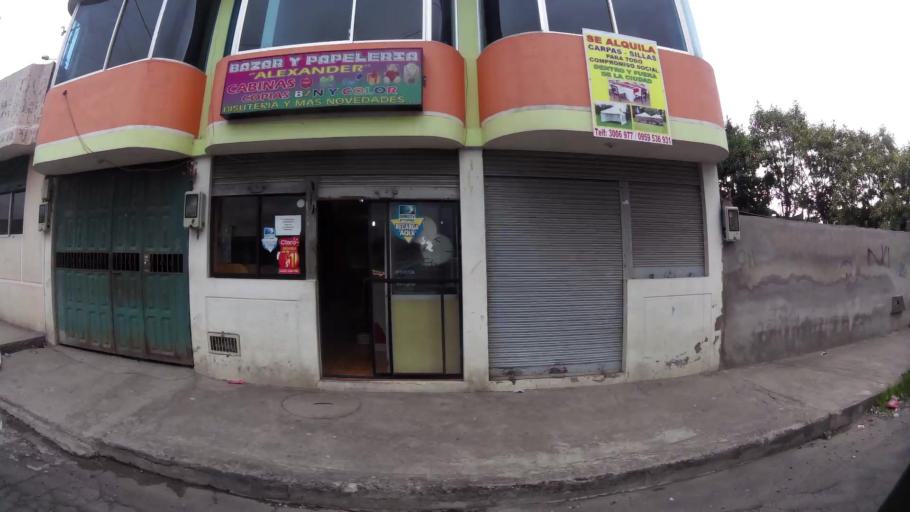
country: EC
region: Pichincha
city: Sangolqui
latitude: -0.3371
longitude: -78.5537
